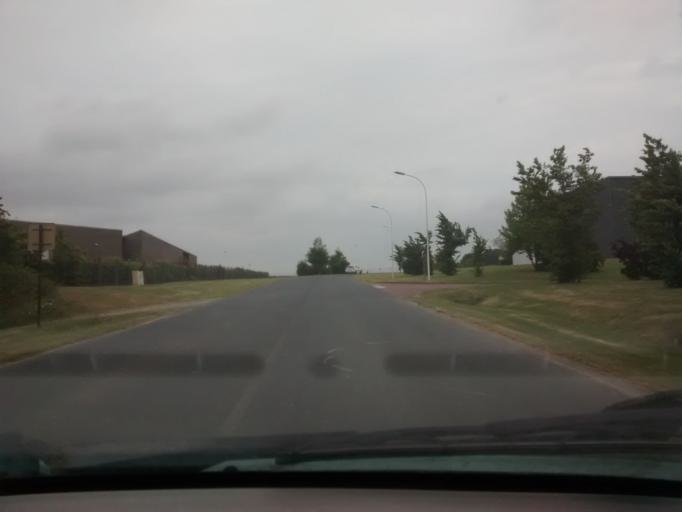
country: FR
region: Lower Normandy
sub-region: Departement de la Manche
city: Saint-Lo
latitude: 49.0975
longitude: -1.0707
